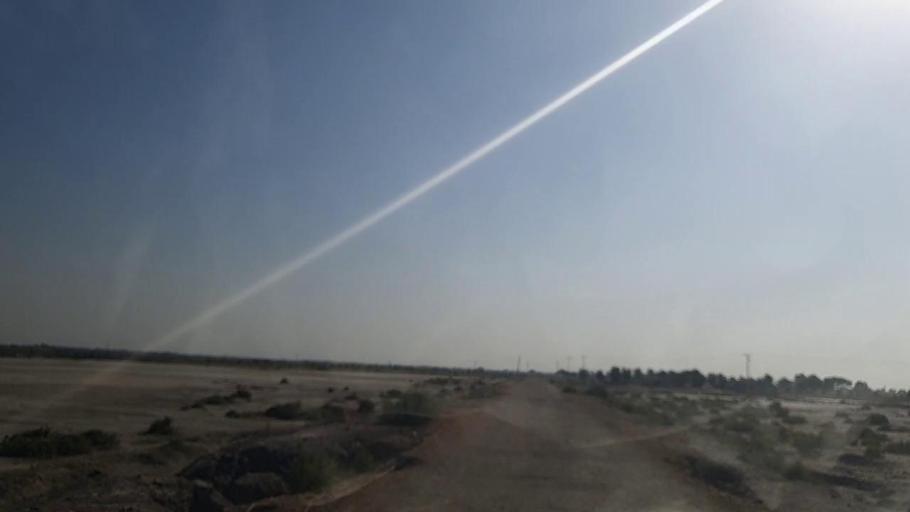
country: PK
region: Sindh
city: Mirpur Batoro
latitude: 24.5939
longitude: 68.1711
